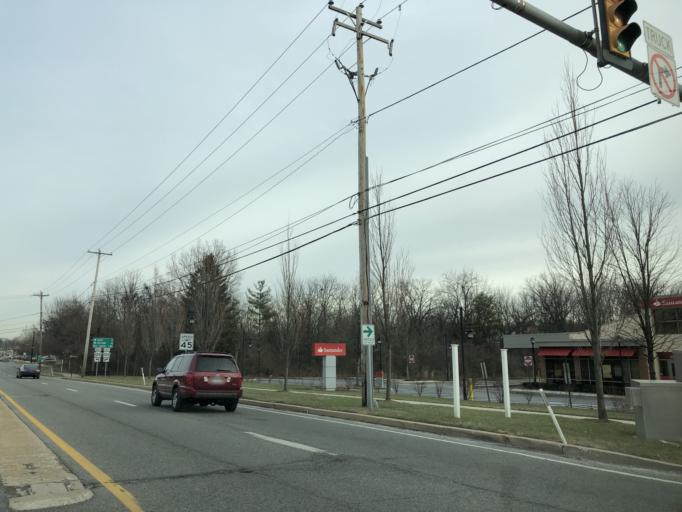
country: US
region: Pennsylvania
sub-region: Chester County
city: Exton
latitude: 40.0274
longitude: -75.6319
